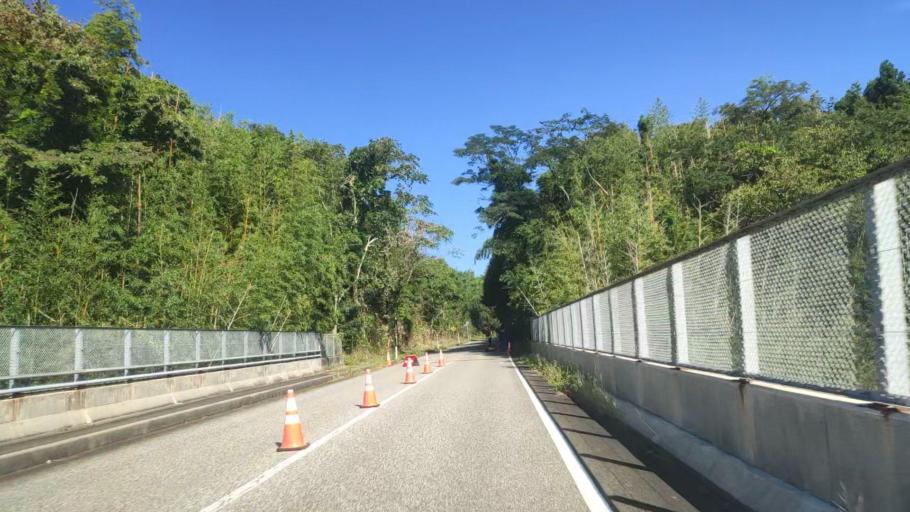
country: JP
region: Ishikawa
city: Hakui
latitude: 37.0876
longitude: 136.7287
